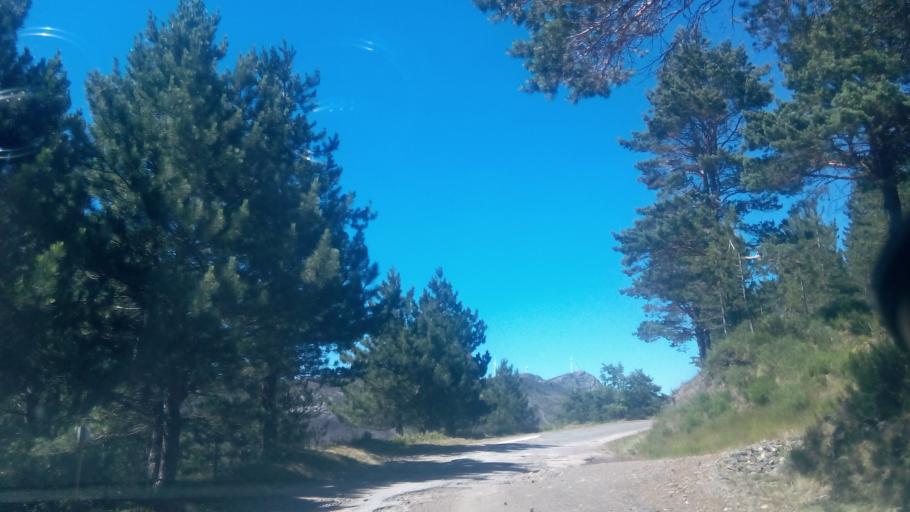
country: PT
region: Vila Real
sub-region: Mesao Frio
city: Mesao Frio
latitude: 41.2729
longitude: -7.9218
